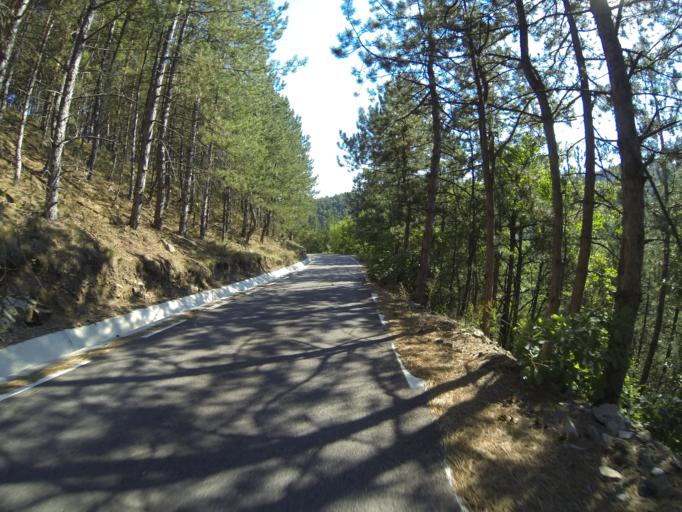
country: RO
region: Mehedinti
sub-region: Comuna Svinita
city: Svinita
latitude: 44.5390
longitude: 22.1935
